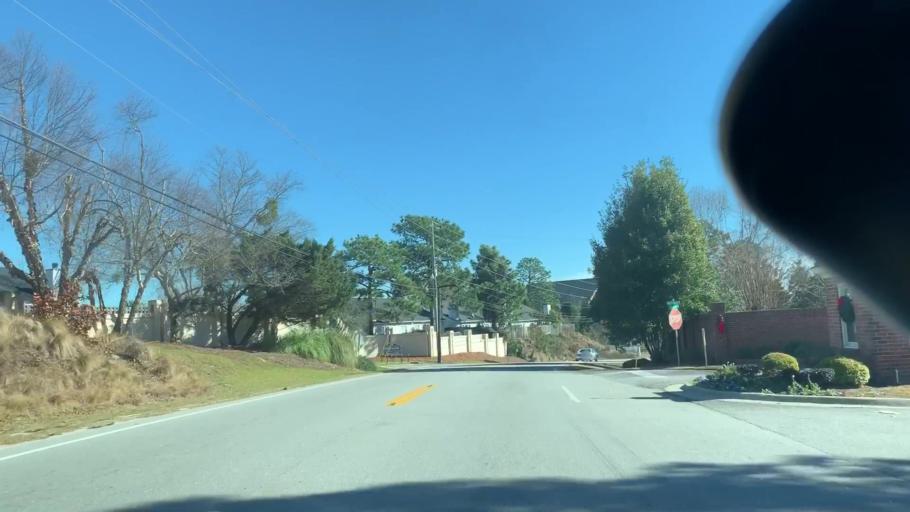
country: US
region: South Carolina
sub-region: Richland County
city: Woodfield
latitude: 34.1056
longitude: -80.8990
